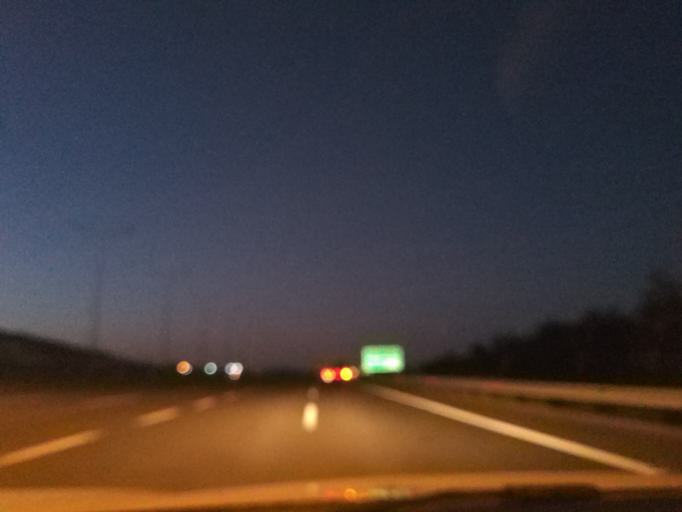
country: TR
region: Istanbul
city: Sancaktepe
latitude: 41.0471
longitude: 29.2769
